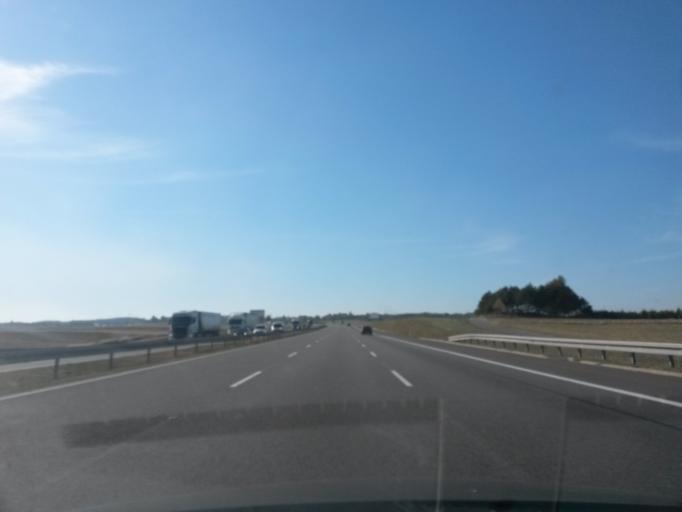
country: PL
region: Opole Voivodeship
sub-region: Powiat strzelecki
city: Lesnica
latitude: 50.4669
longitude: 18.1849
